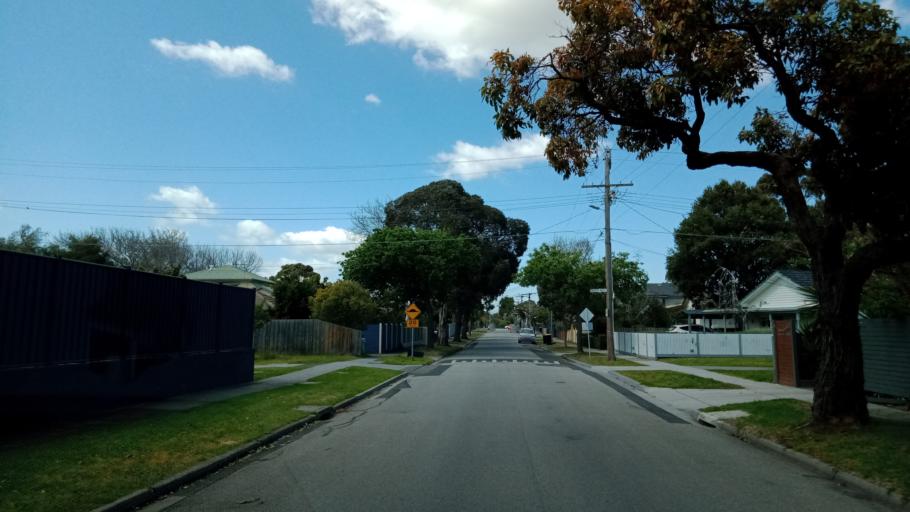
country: AU
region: Victoria
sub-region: Kingston
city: Chelsea Heights
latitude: -38.0433
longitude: 145.1347
